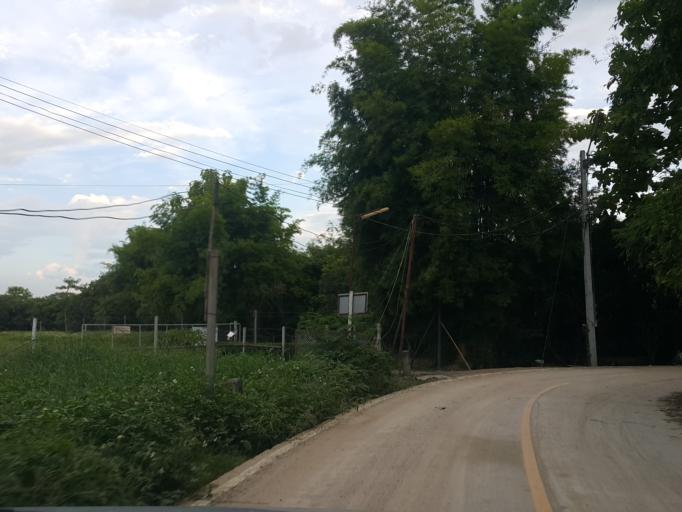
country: TH
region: Chiang Mai
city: San Sai
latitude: 18.8808
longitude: 99.0907
